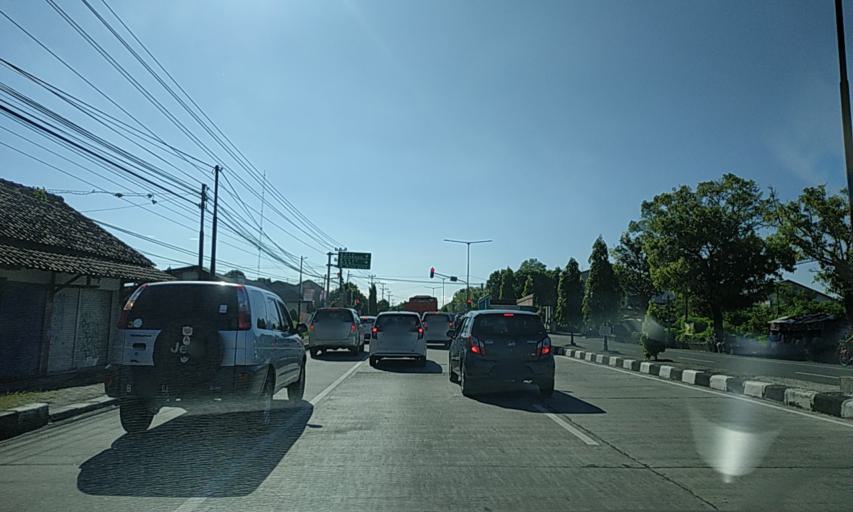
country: ID
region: Central Java
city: Kebonarun
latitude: -7.7183
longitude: 110.5774
